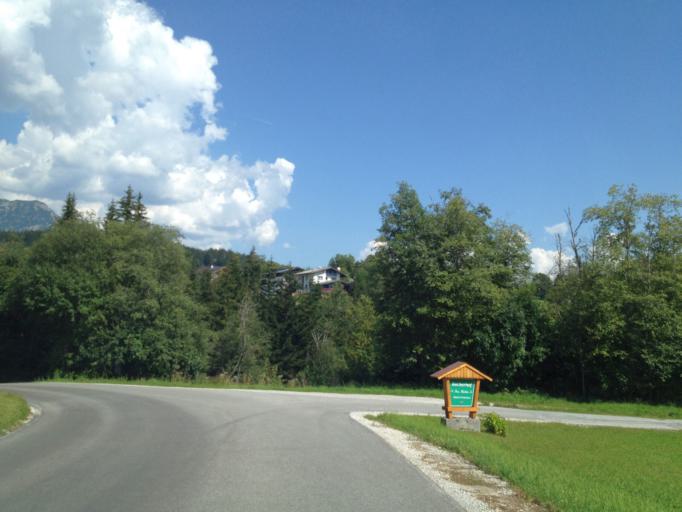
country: AT
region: Styria
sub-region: Politischer Bezirk Liezen
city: Schladming
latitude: 47.4065
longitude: 13.6278
